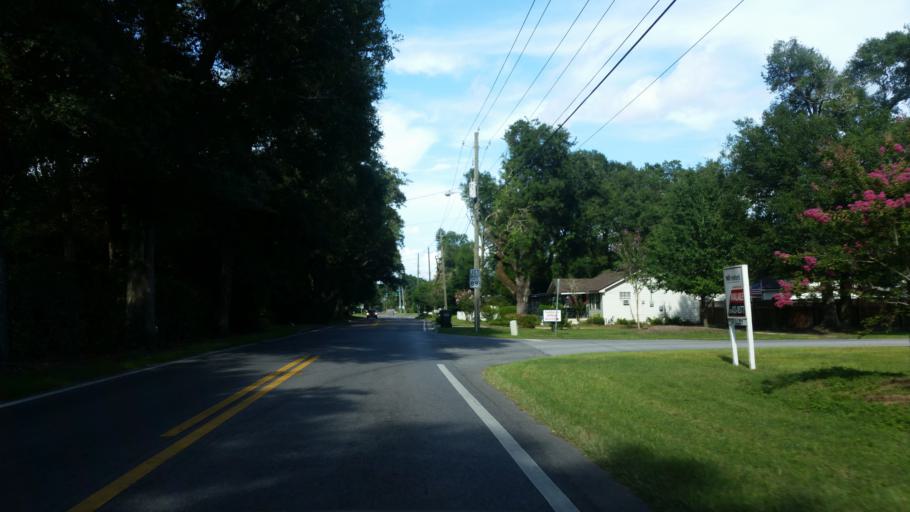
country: US
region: Florida
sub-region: Santa Rosa County
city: Milton
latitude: 30.6226
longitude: -87.0585
